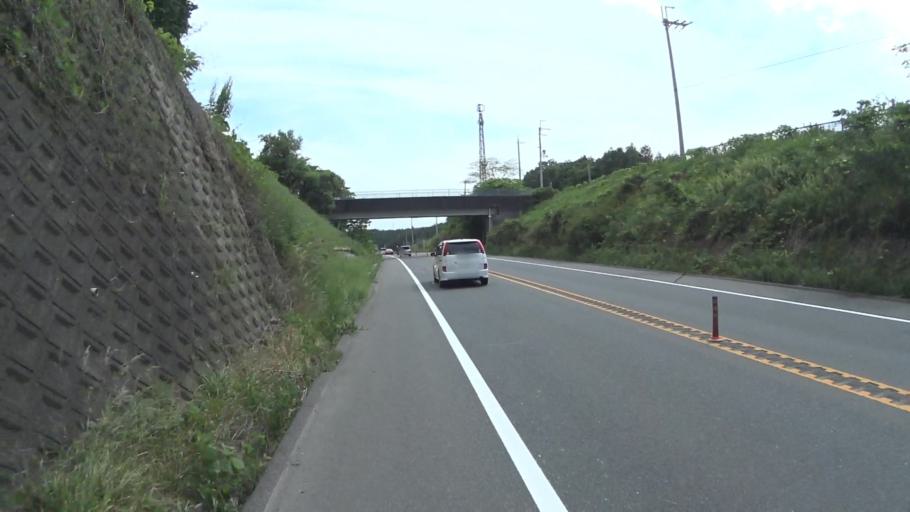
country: JP
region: Shiga Prefecture
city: Kitahama
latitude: 35.1258
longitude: 135.9000
